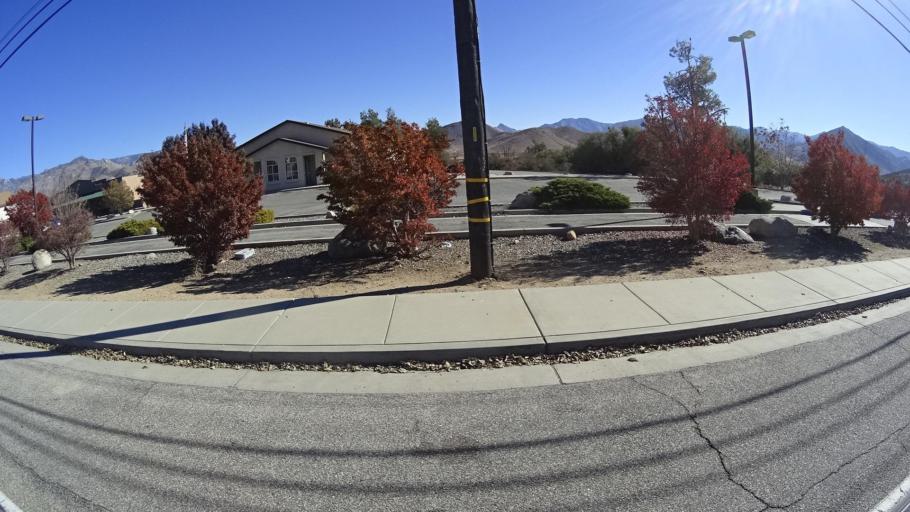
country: US
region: California
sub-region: Kern County
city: Wofford Heights
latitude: 35.7039
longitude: -118.4580
